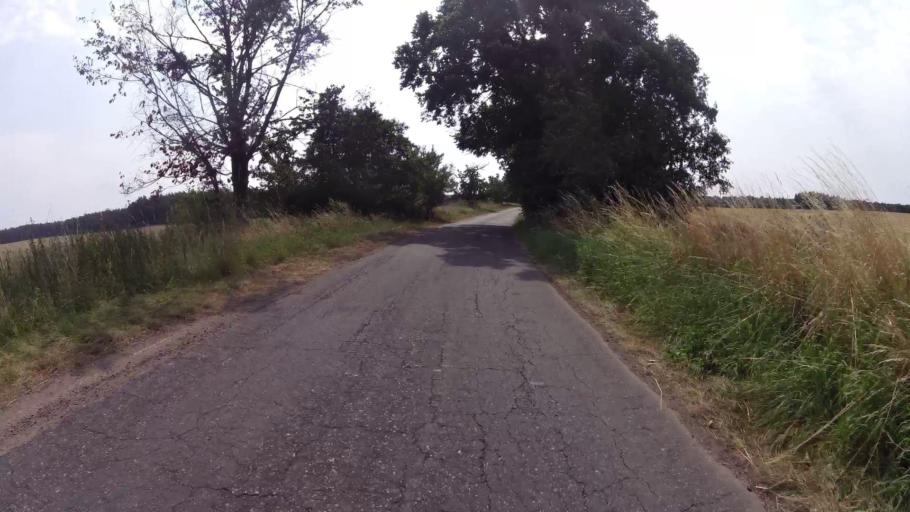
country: PL
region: West Pomeranian Voivodeship
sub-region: Powiat gryfinski
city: Mieszkowice
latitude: 52.8801
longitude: 14.5278
